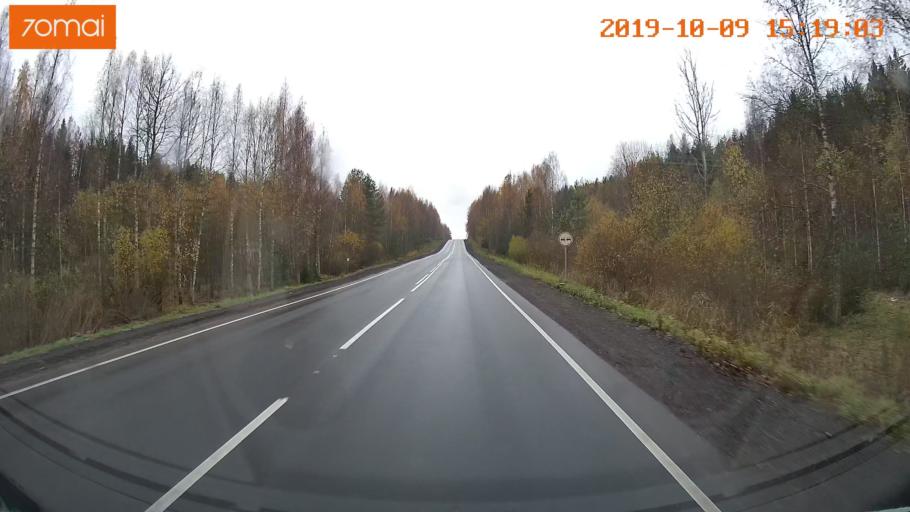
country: RU
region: Kostroma
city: Susanino
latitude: 58.0798
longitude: 41.5631
